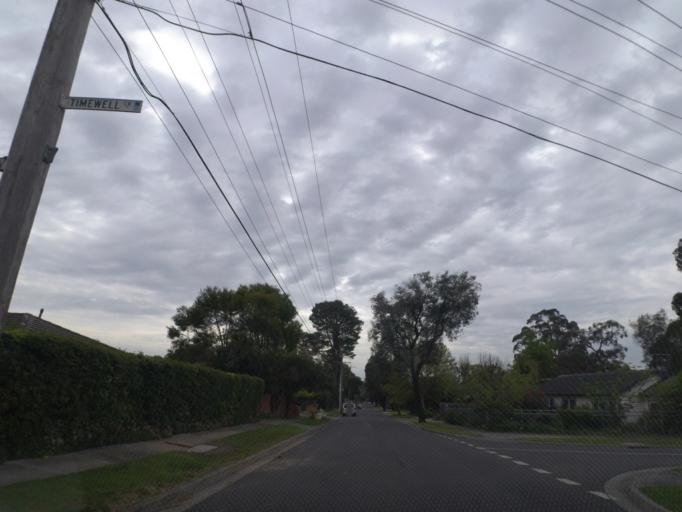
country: AU
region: Victoria
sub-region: Knox
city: The Basin
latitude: -37.8570
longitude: 145.3000
